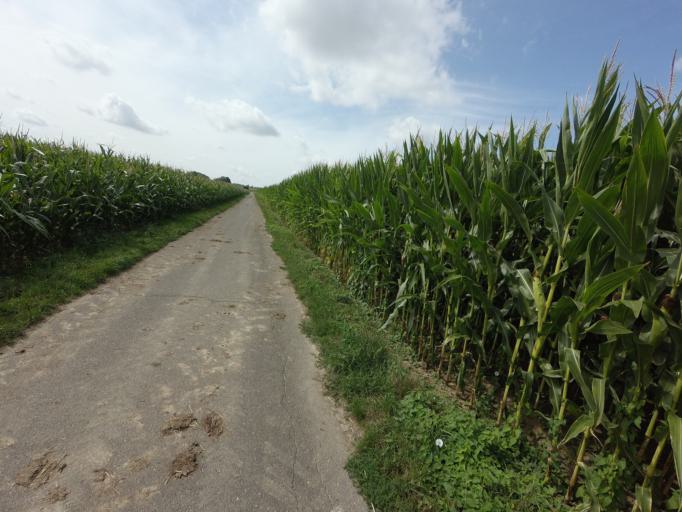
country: DE
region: North Rhine-Westphalia
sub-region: Regierungsbezirk Koln
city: Ubach-Palenberg
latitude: 50.9348
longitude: 6.0591
